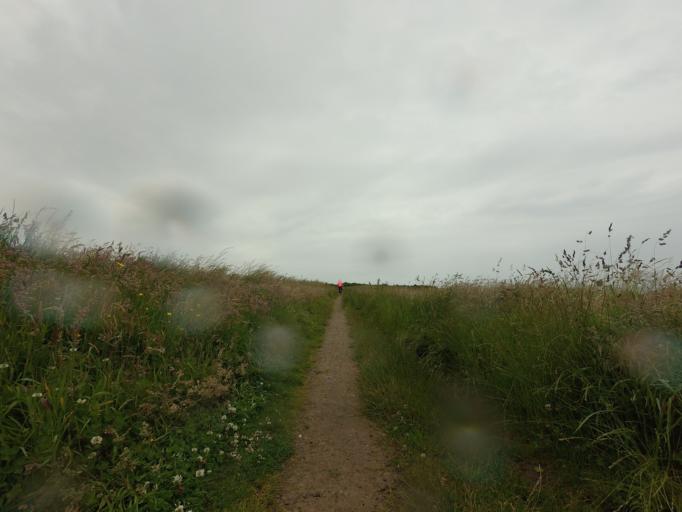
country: GB
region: Scotland
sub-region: Moray
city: Portknockie
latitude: 57.7026
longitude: -2.8672
